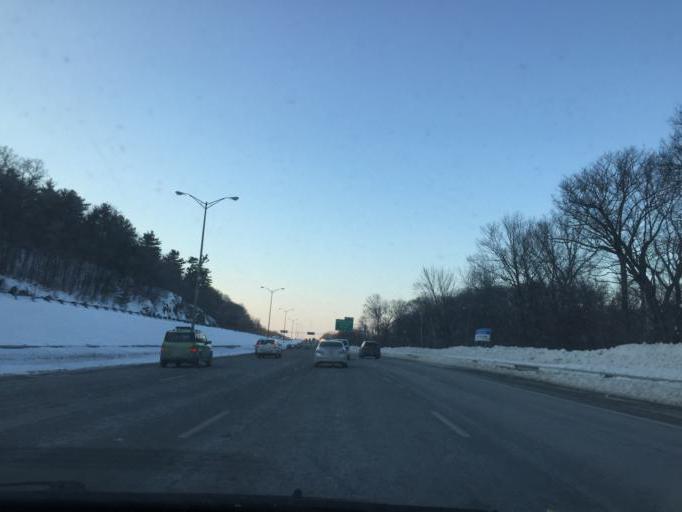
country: US
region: Massachusetts
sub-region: Middlesex County
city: Stoneham
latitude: 42.4639
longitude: -71.1033
